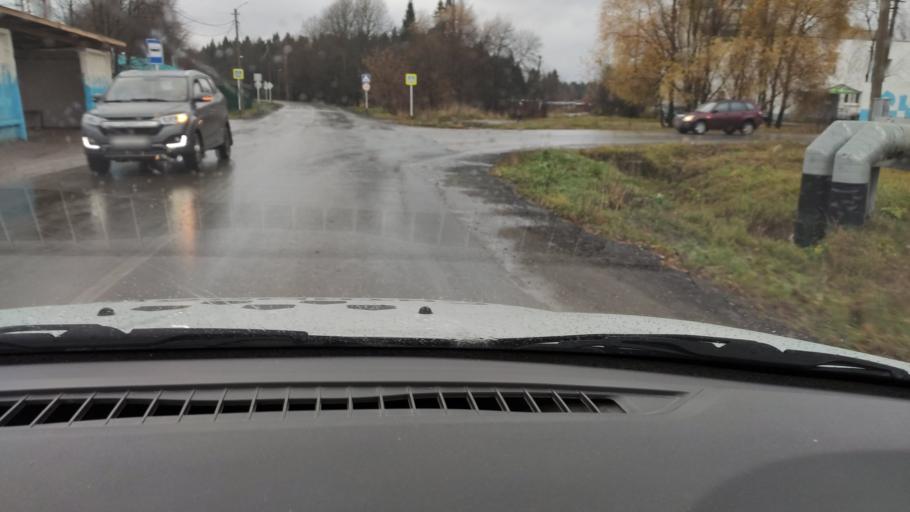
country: RU
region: Perm
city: Sylva
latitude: 58.0302
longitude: 56.7406
